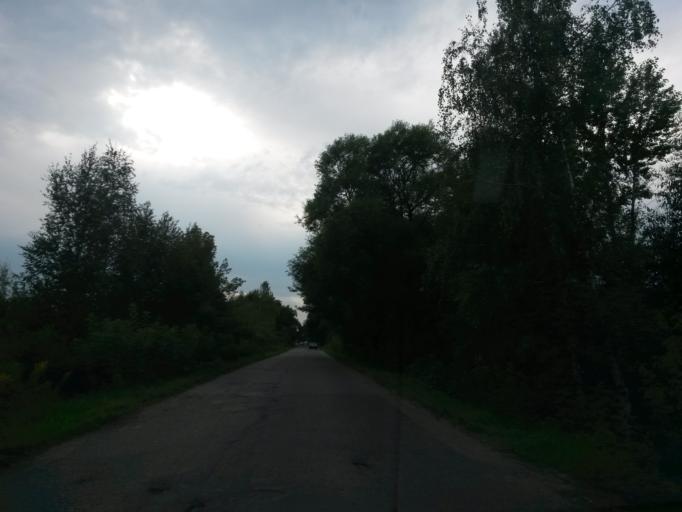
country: RU
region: Jaroslavl
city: Yaroslavl
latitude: 57.6077
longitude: 39.7834
